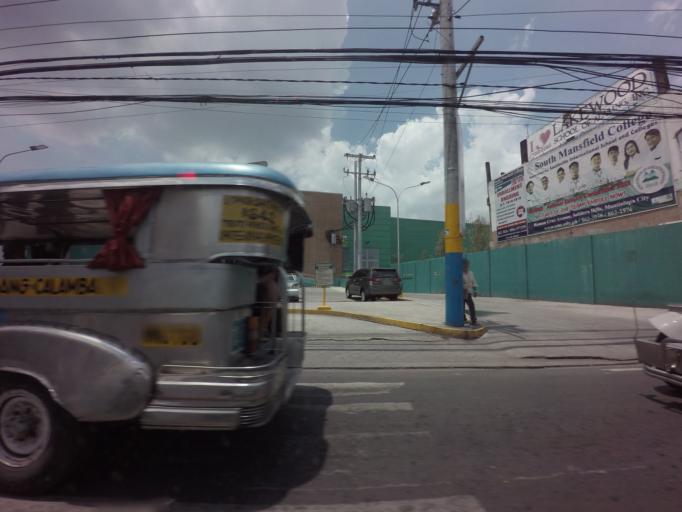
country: PH
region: Calabarzon
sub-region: Province of Laguna
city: San Pedro
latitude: 14.3985
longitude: 121.0460
